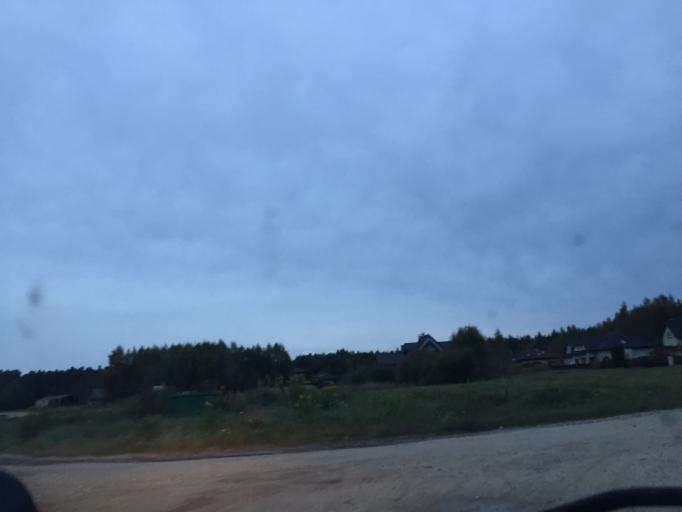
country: LV
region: Adazi
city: Adazi
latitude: 57.0869
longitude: 24.3749
